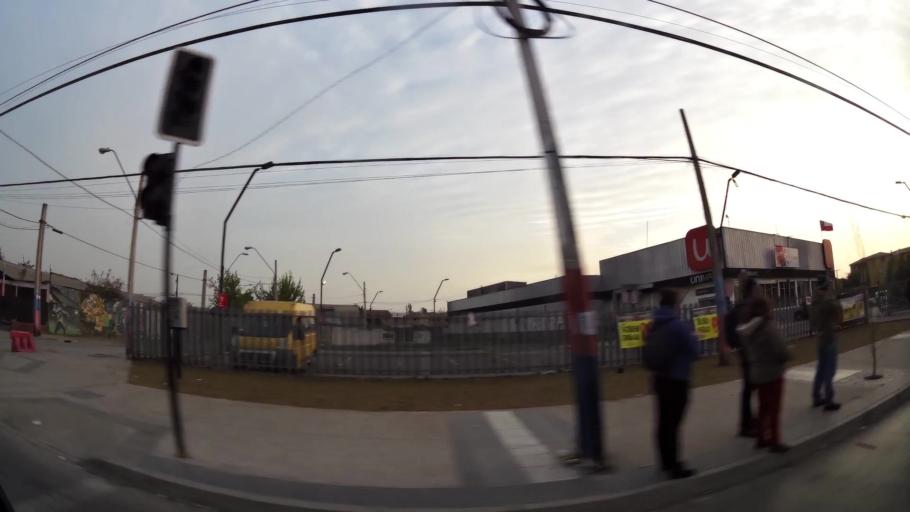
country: CL
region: Santiago Metropolitan
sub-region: Provincia de Santiago
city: Lo Prado
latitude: -33.5074
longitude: -70.7832
